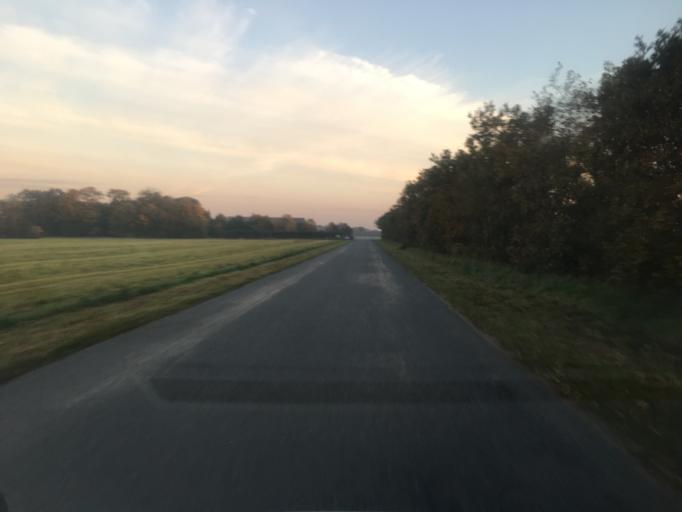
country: DK
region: South Denmark
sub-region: Tonder Kommune
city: Logumkloster
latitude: 55.0138
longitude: 9.0477
